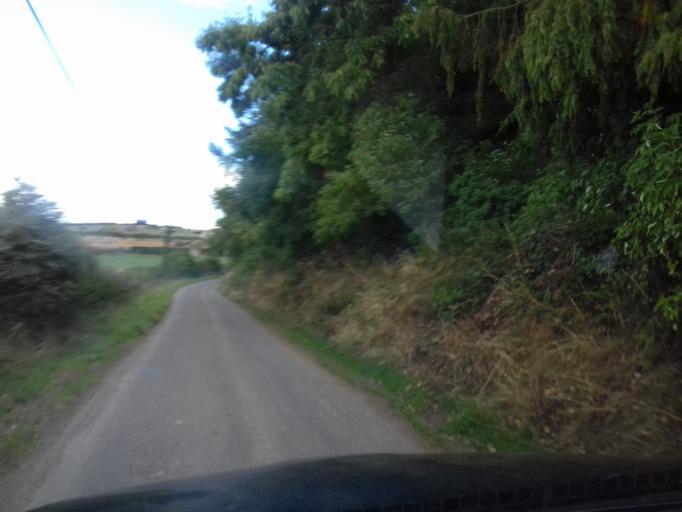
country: IE
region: Leinster
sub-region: Kilkenny
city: Graiguenamanagh
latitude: 52.5817
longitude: -7.0105
